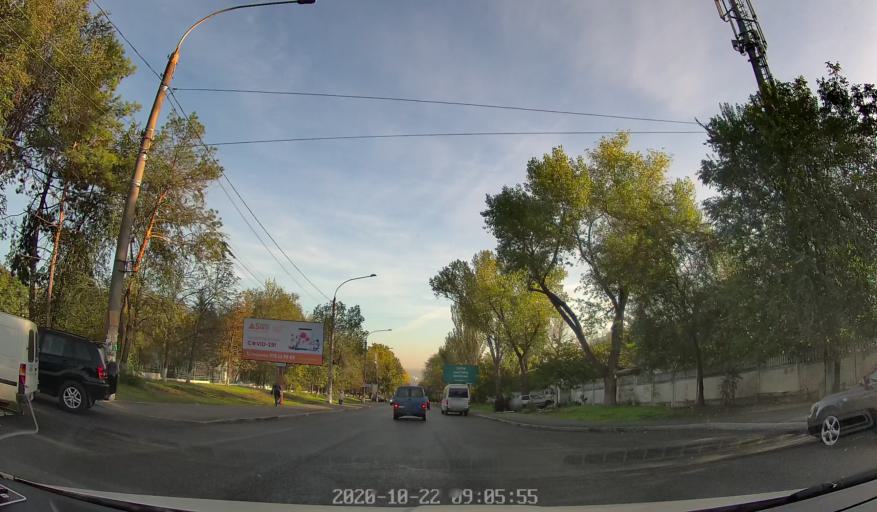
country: MD
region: Chisinau
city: Chisinau
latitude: 46.9916
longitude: 28.8285
